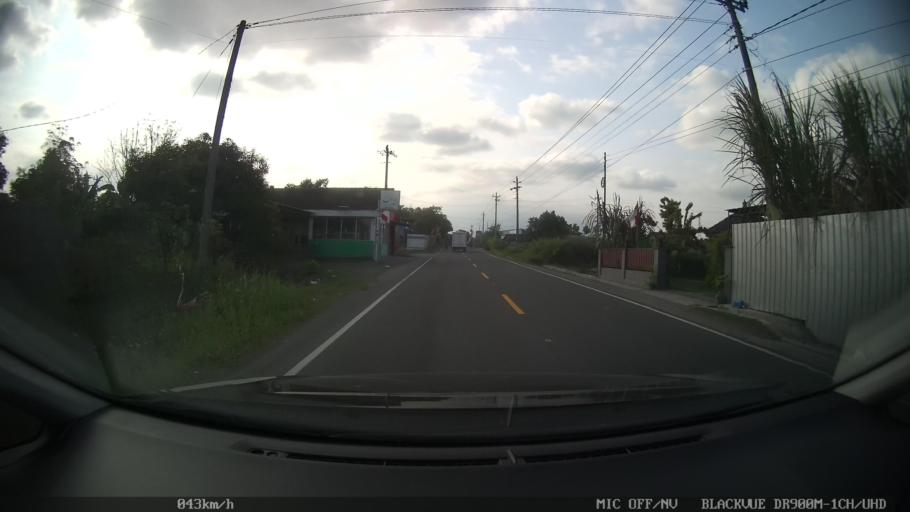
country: ID
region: Central Java
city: Candi Prambanan
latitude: -7.7172
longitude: 110.4727
